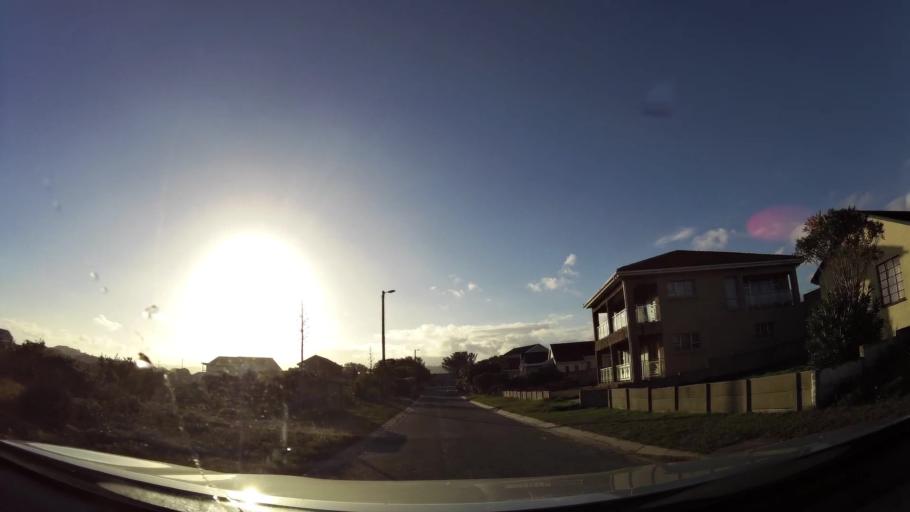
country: ZA
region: Western Cape
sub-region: Eden District Municipality
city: George
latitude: -34.0041
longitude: 22.6560
